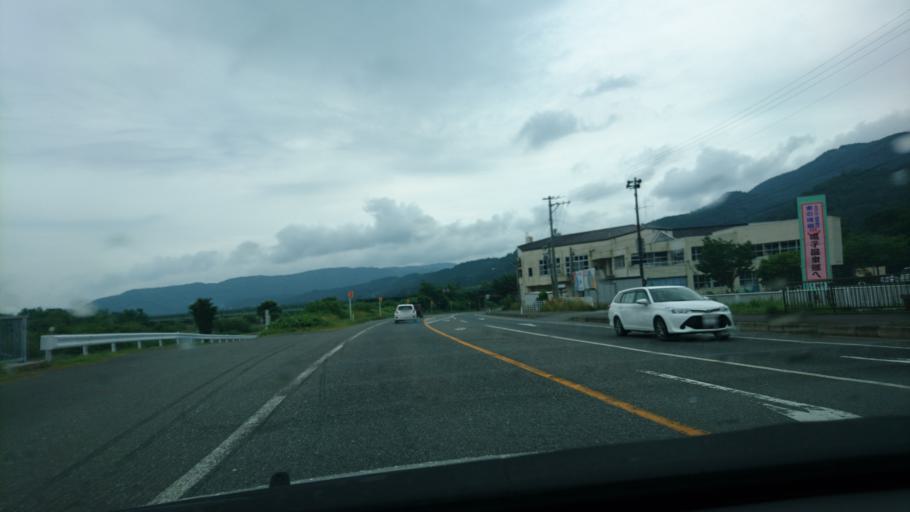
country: JP
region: Miyagi
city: Furukawa
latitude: 38.7460
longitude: 140.7378
